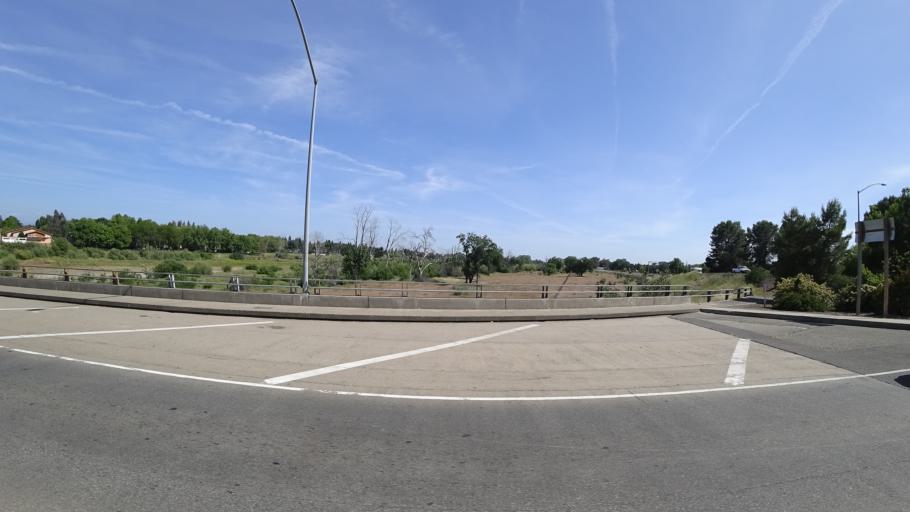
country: US
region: California
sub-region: Tehama County
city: Red Bluff
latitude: 40.1814
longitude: -122.2234
